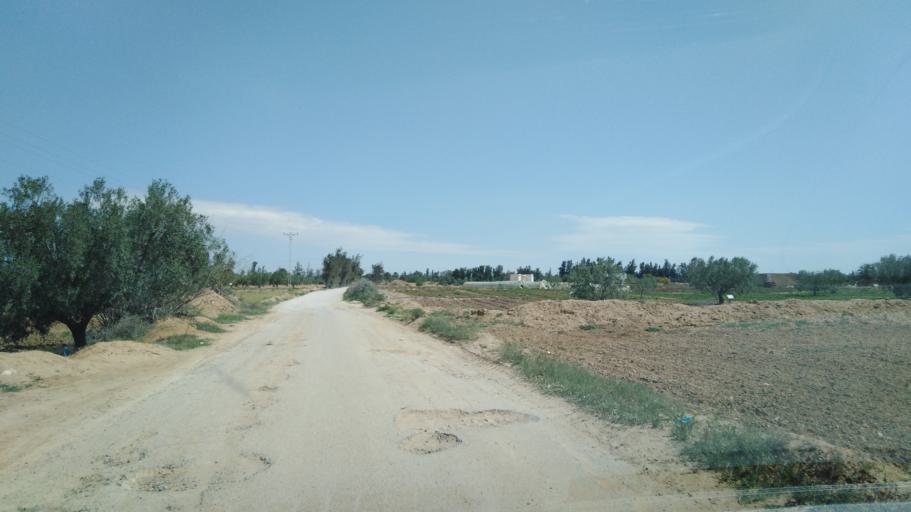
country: TN
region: Safaqis
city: Sfax
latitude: 34.7539
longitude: 10.5285
